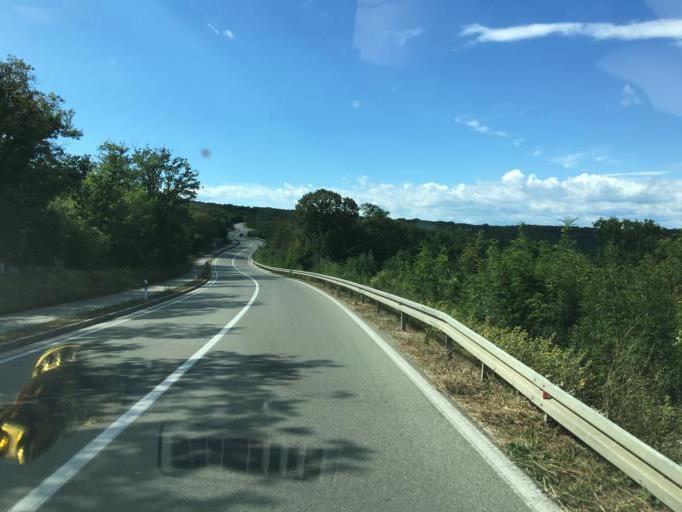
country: HR
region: Primorsko-Goranska
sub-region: Grad Krk
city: Krk
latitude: 45.0752
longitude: 14.5489
